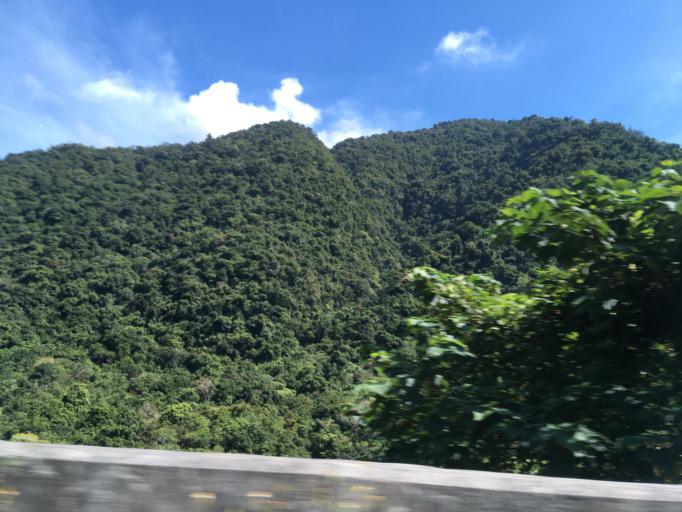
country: TW
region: Taiwan
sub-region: Yilan
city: Yilan
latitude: 24.4206
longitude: 121.7311
